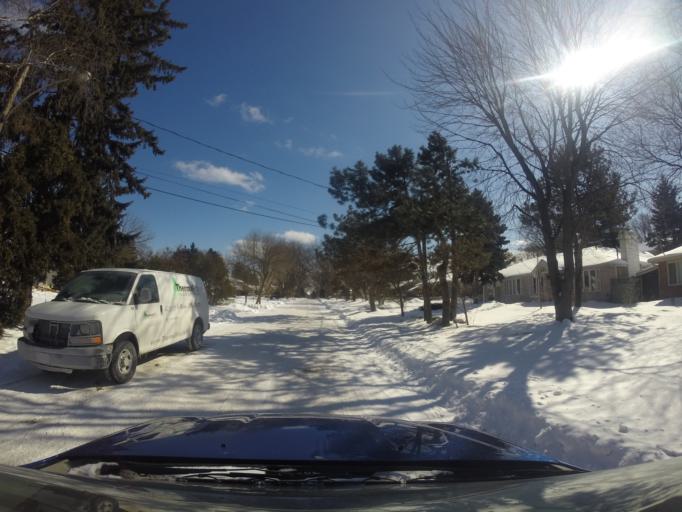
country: CA
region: Ontario
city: Burlington
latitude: 43.3452
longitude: -79.7672
